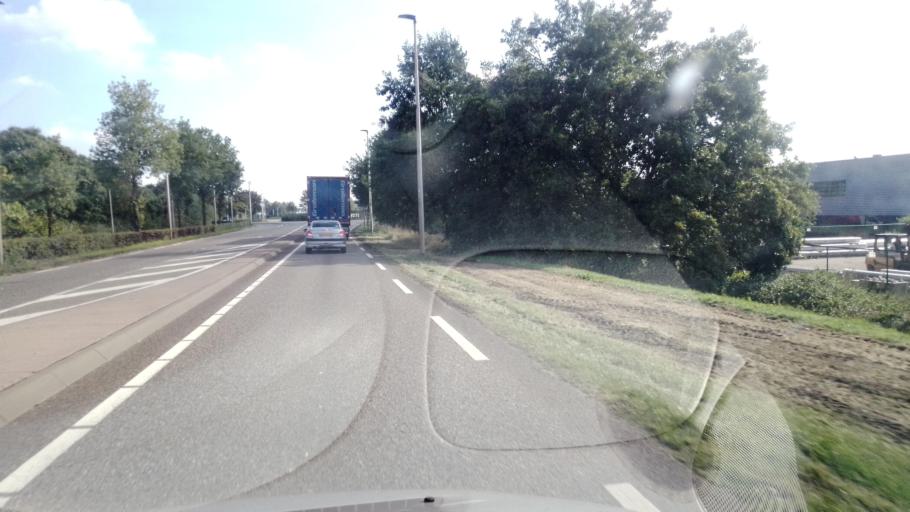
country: NL
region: North Brabant
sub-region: Gemeente Helmond
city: Helmond
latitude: 51.4521
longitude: 5.6985
